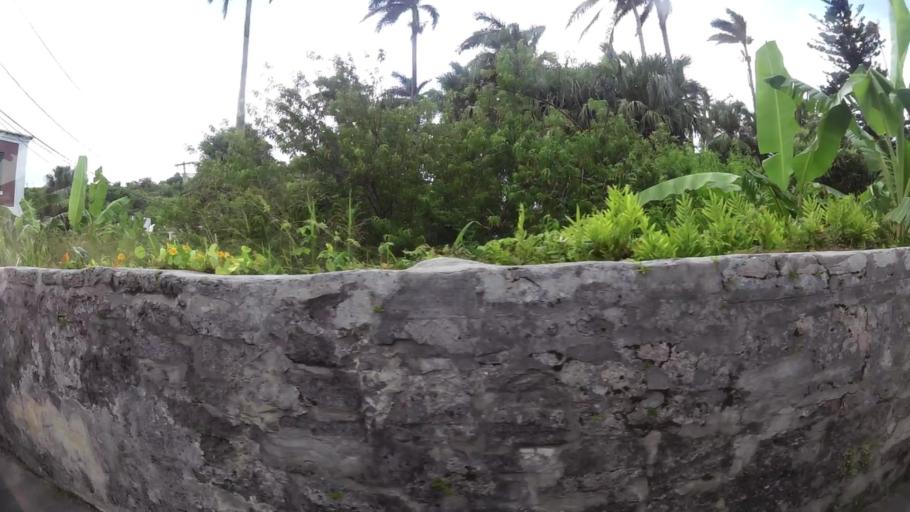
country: BM
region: Saint George
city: Saint George
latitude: 32.3823
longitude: -64.6766
